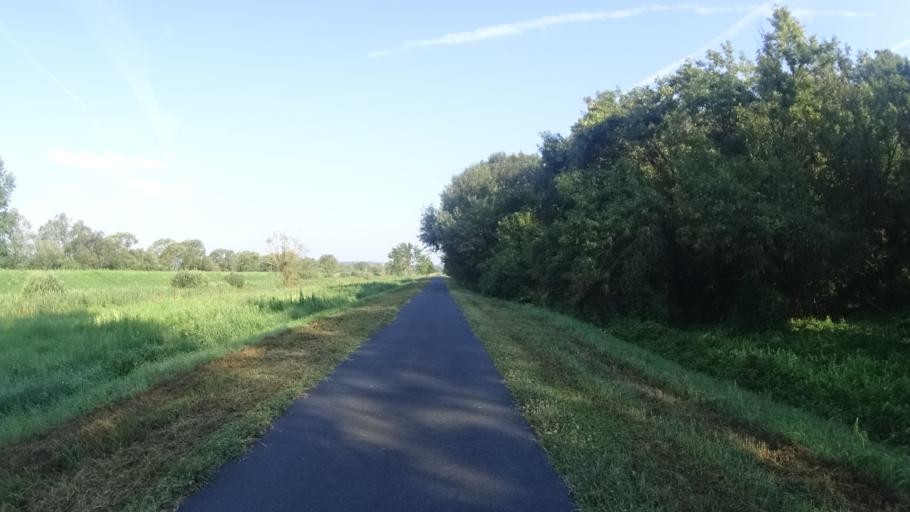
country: HU
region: Zala
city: Sarmellek
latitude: 46.6487
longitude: 17.1512
